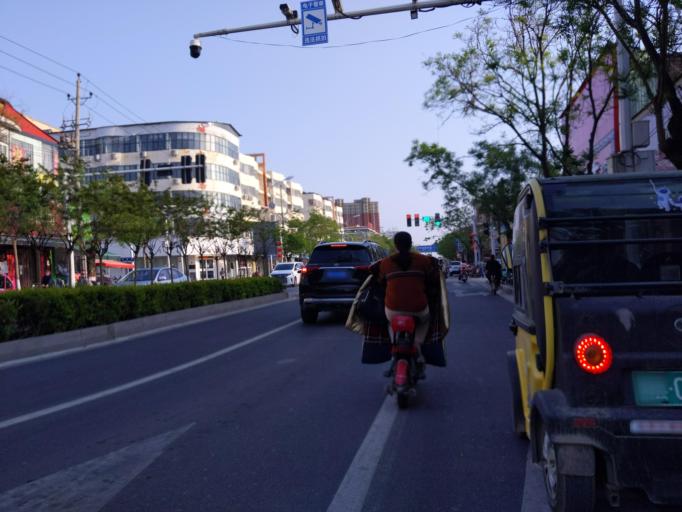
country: CN
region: Henan Sheng
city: Puyang Chengguanzhen
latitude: 35.7018
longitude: 115.0163
